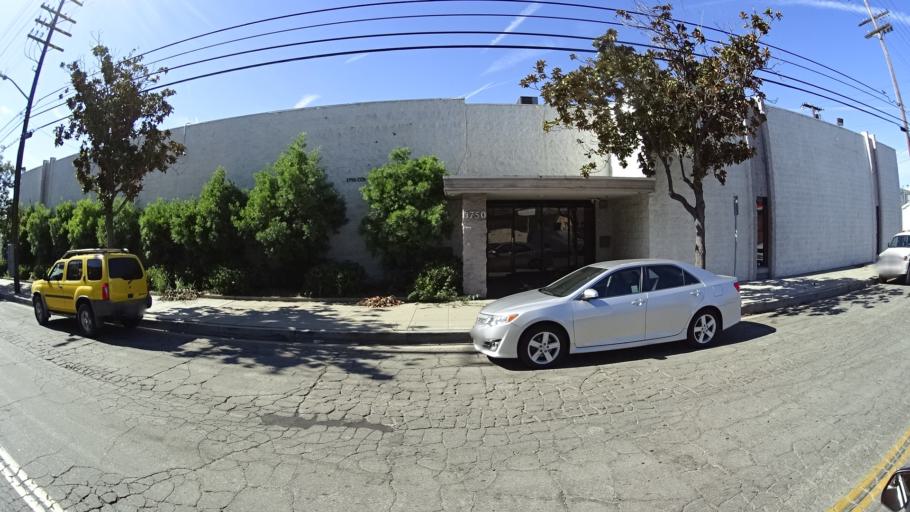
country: US
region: California
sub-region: Los Angeles County
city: North Hollywood
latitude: 34.2067
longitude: -118.3516
